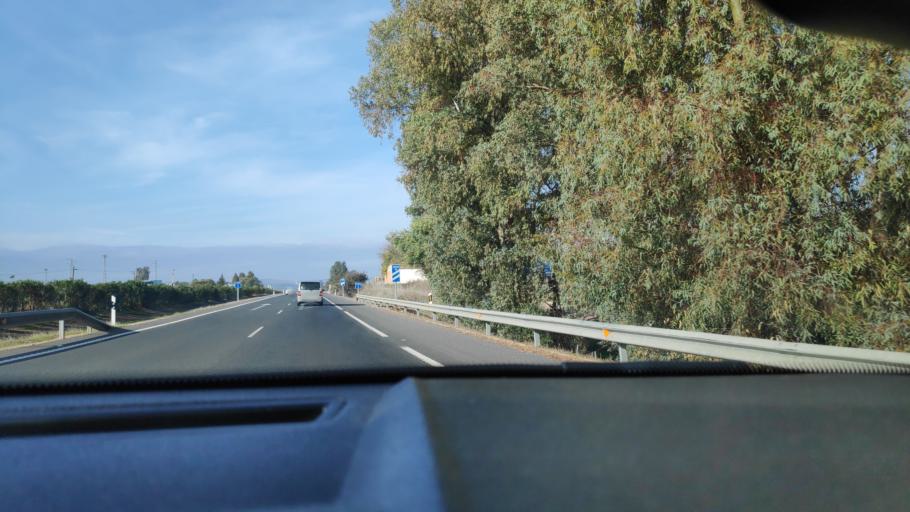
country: ES
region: Andalusia
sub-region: Provincia de Jaen
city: Linares
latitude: 38.0952
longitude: -3.6943
